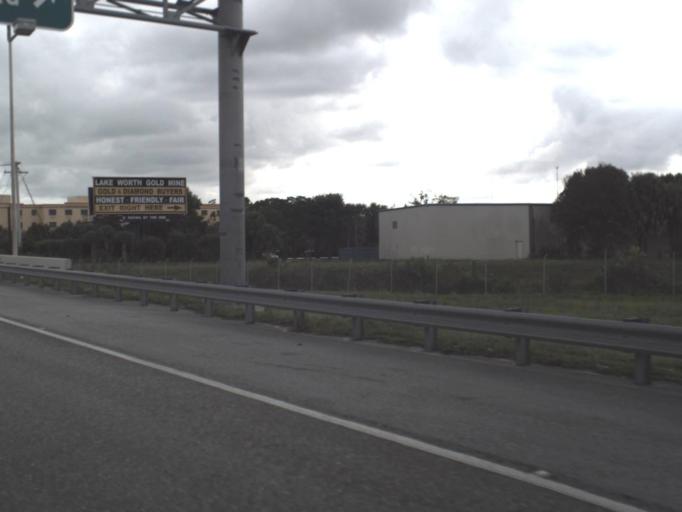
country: US
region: Florida
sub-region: Palm Beach County
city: Greenacres City
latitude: 26.6207
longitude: -80.1739
